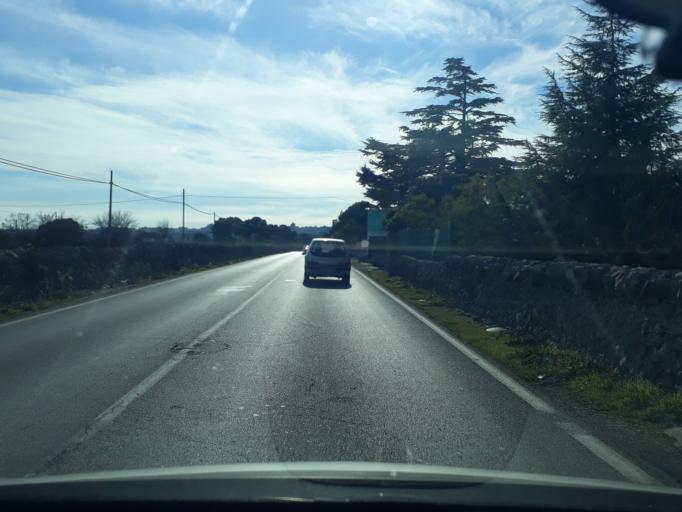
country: IT
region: Apulia
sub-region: Provincia di Taranto
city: Martina Franca
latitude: 40.7271
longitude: 17.3326
